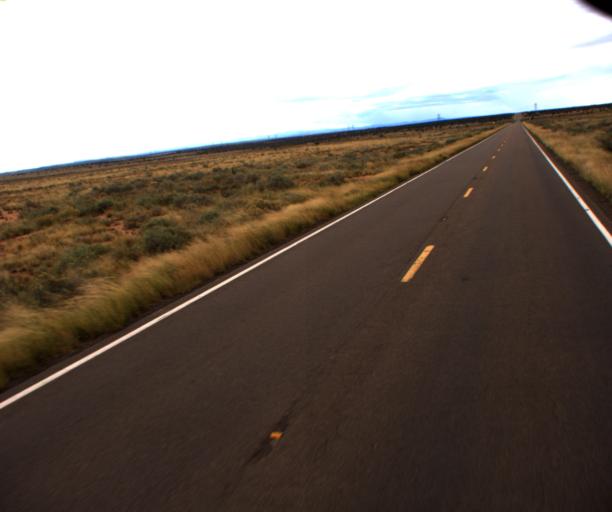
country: US
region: Arizona
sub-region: Navajo County
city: Snowflake
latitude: 34.6626
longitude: -110.1004
